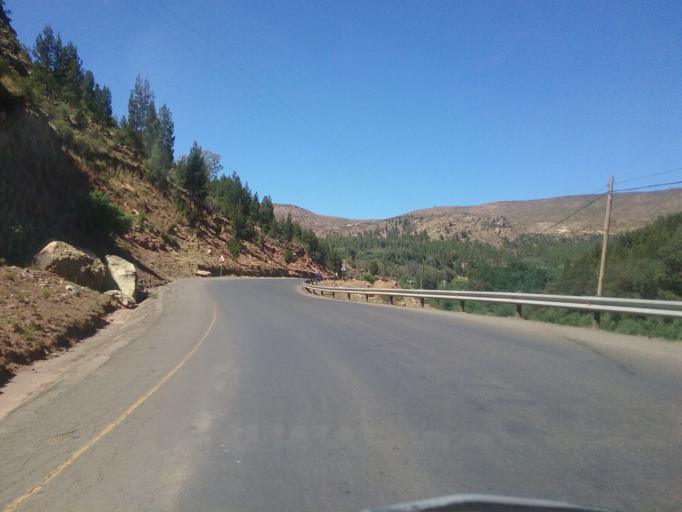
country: LS
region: Quthing
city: Quthing
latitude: -30.3990
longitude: 27.6862
